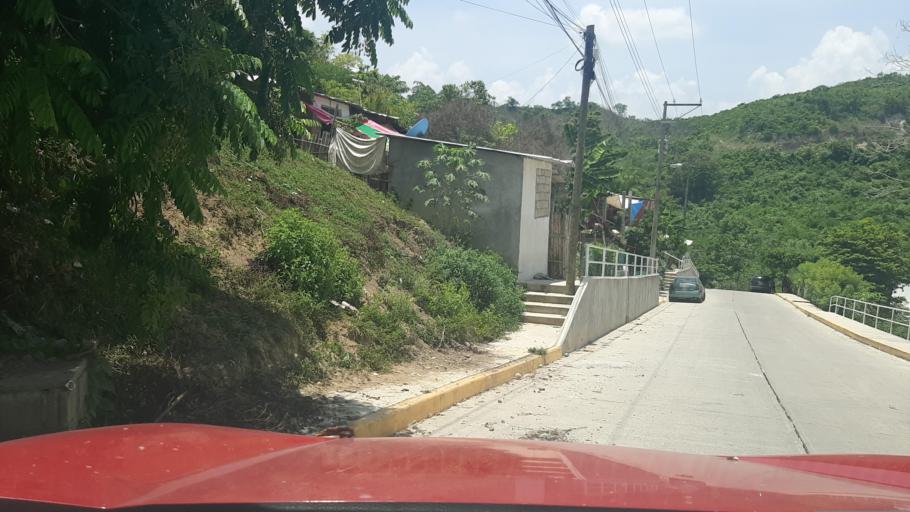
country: MX
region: Veracruz
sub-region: Poza Rica de Hidalgo
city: Arroyo del Maiz Uno
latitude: 20.4984
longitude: -97.4225
